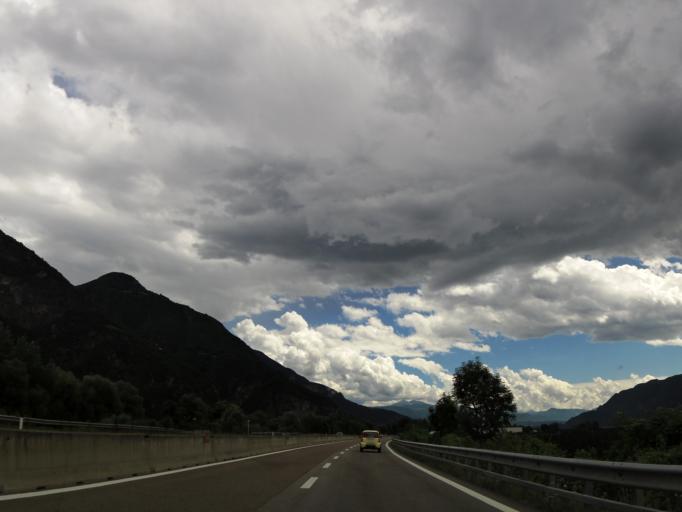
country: IT
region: Trentino-Alto Adige
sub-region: Bolzano
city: Gargazzone
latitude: 46.5672
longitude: 11.2111
